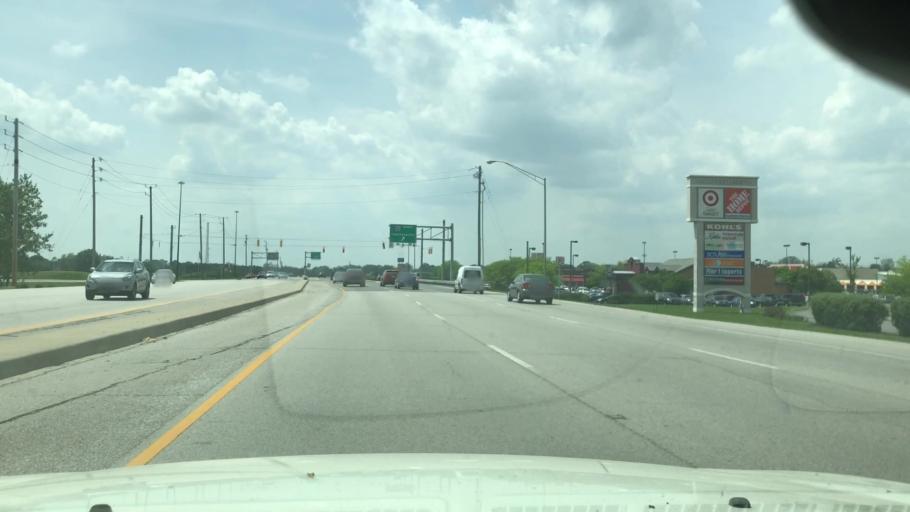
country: US
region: Indiana
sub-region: Marion County
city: Southport
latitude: 39.6660
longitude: -86.0846
